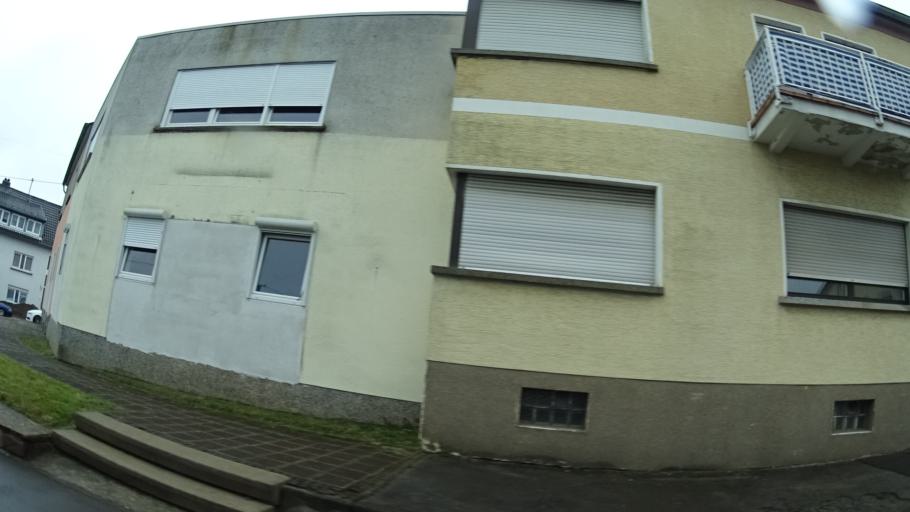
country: DE
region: Saarland
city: Heusweiler
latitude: 49.3313
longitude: 6.9895
